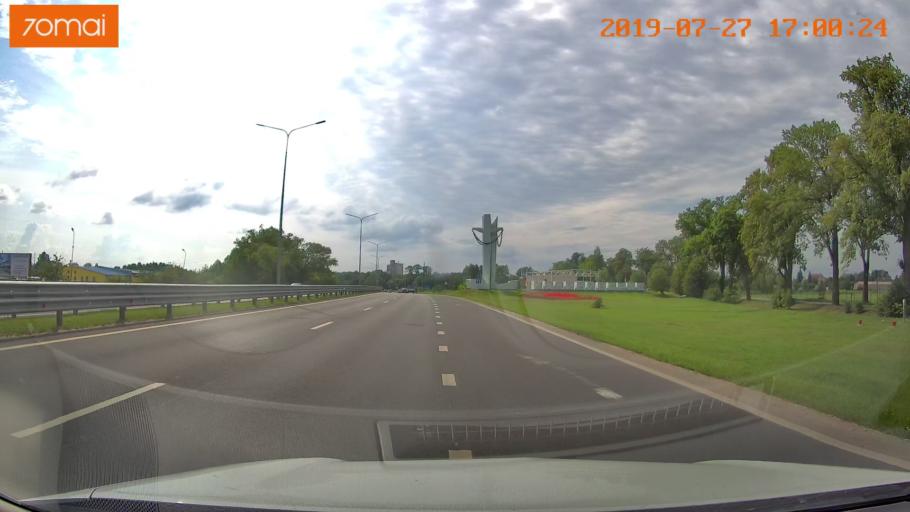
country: RU
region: Kaliningrad
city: Bol'shoe Isakovo
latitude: 54.7077
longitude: 20.6274
